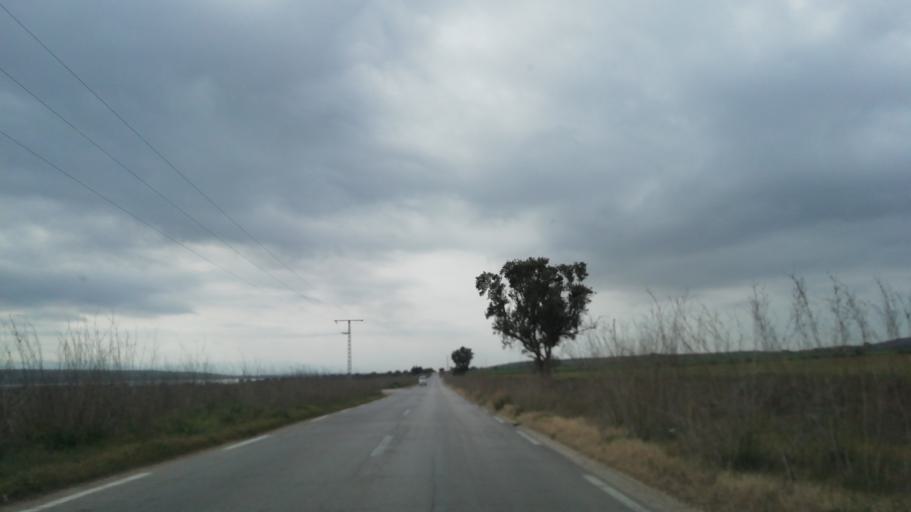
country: DZ
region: Oran
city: Sidi ech Chahmi
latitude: 35.6209
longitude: -0.4120
